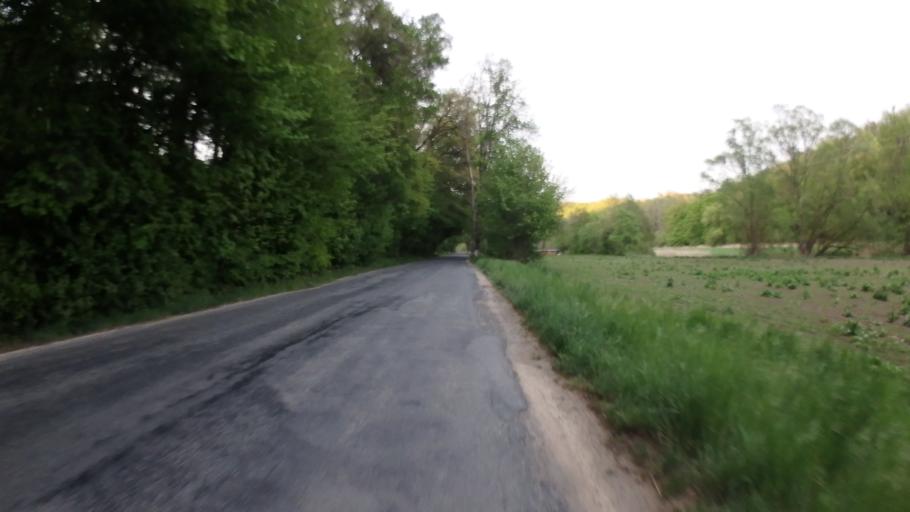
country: CZ
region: South Moravian
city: Strelice
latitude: 49.1419
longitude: 16.4653
